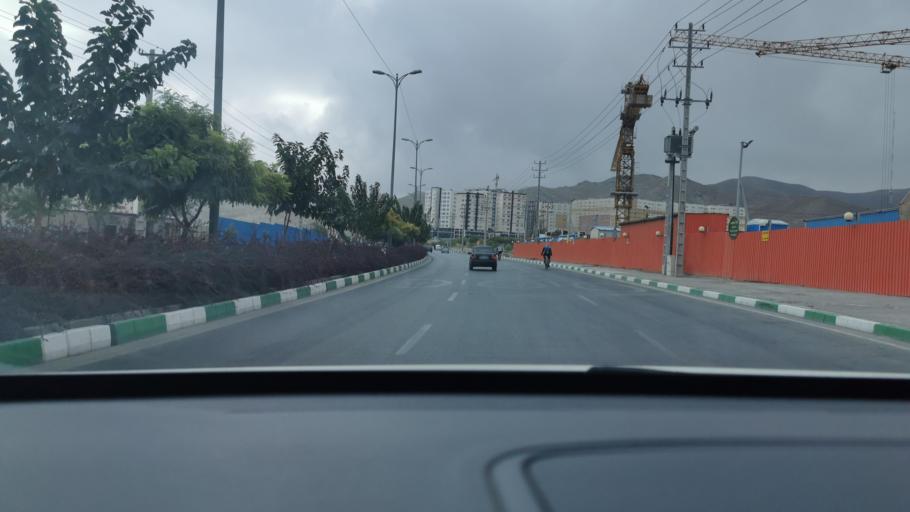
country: IR
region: Razavi Khorasan
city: Mashhad
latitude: 36.2723
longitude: 59.5384
